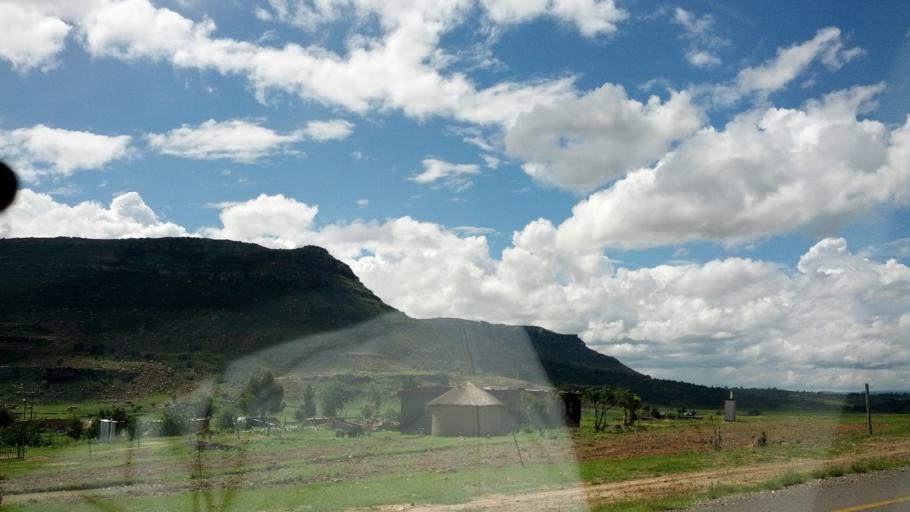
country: LS
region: Maseru
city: Maseru
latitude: -29.5334
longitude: 27.5111
